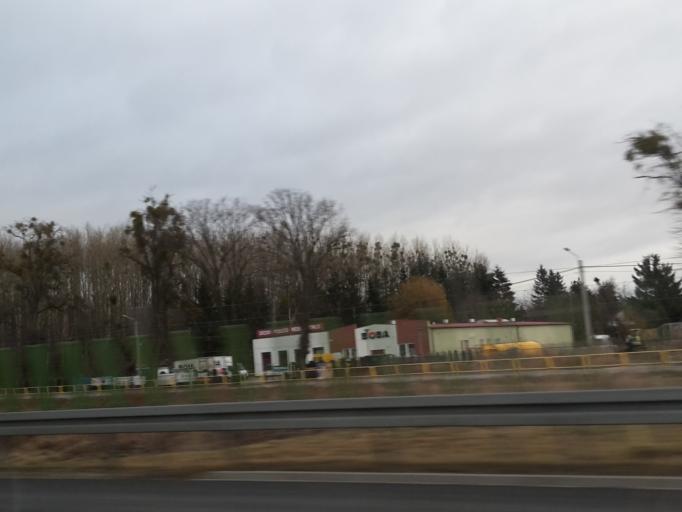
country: PL
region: Warmian-Masurian Voivodeship
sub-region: Powiat elblaski
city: Gronowo Gorne
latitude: 54.1288
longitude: 19.4600
